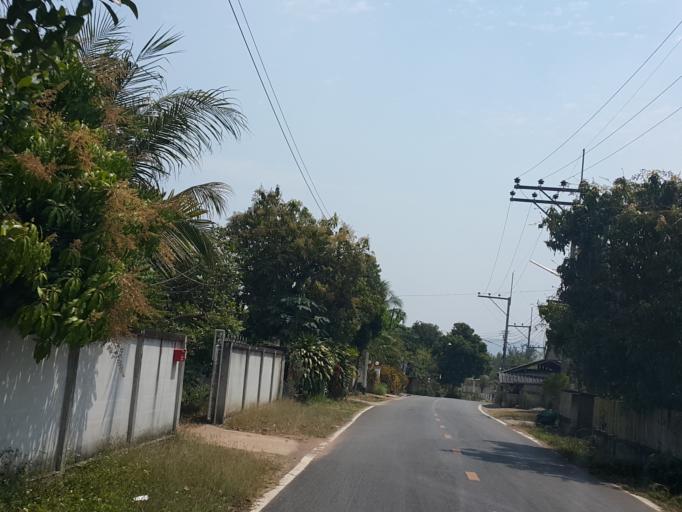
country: TH
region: Lampang
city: Mueang Pan
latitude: 18.7883
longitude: 99.4948
